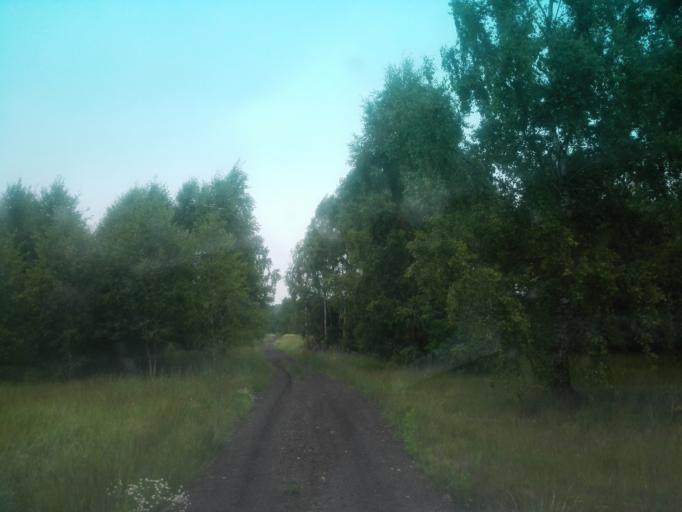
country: PL
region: Silesian Voivodeship
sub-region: Powiat czestochowski
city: Olsztyn
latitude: 50.7899
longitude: 19.2660
